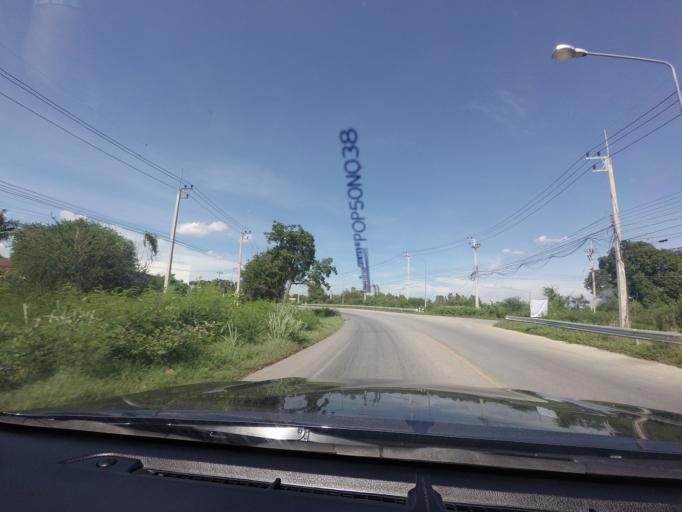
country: TH
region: Suphan Buri
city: Song Phi Nong
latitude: 14.1709
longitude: 99.9320
